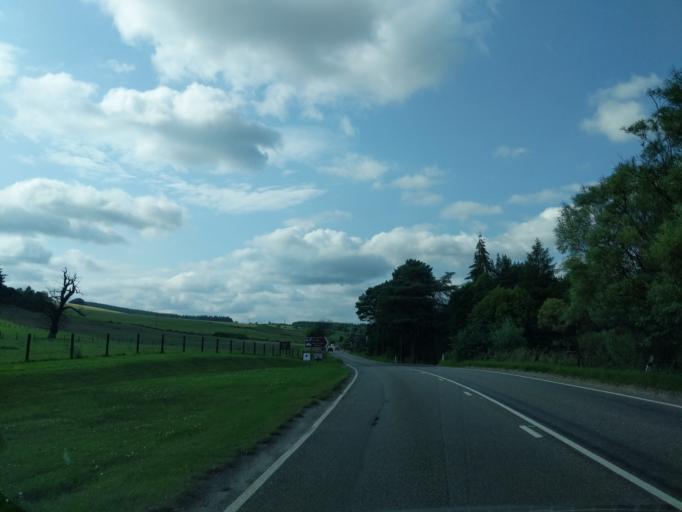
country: GB
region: Scotland
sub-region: Moray
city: Dufftown
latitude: 57.4592
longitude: -3.1322
